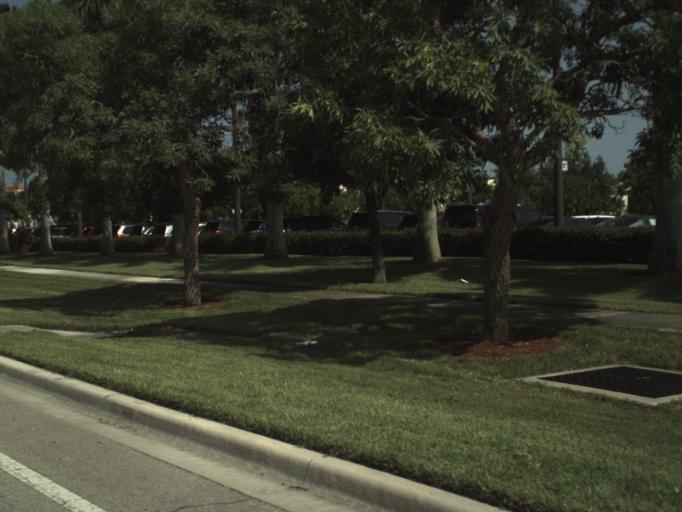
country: US
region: Florida
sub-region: Broward County
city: Tedder
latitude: 26.2745
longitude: -80.1469
